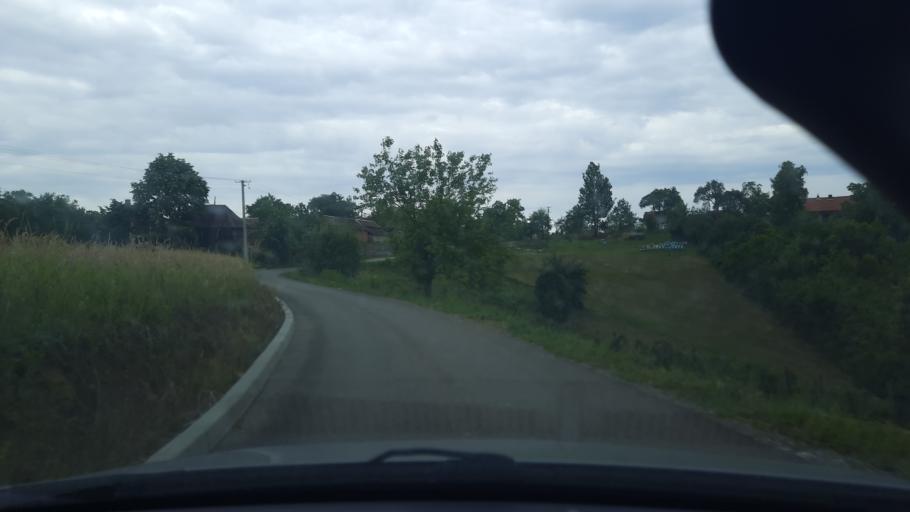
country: RS
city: Jarebice
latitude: 44.5008
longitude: 19.4762
